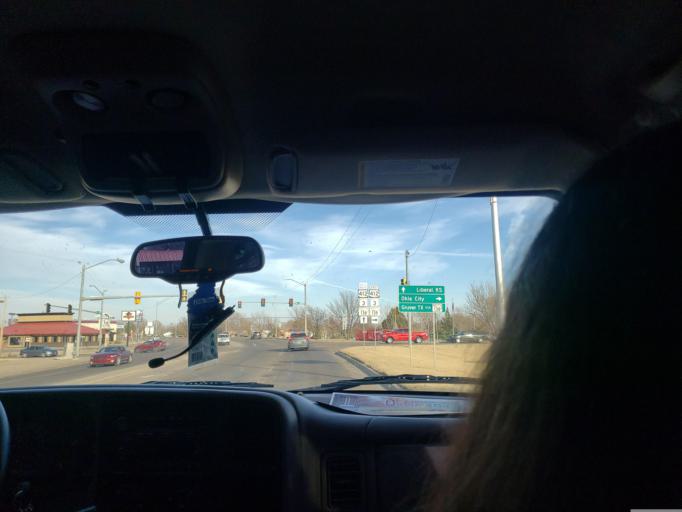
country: US
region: Oklahoma
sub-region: Texas County
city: Guymon
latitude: 36.6776
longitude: -101.4754
